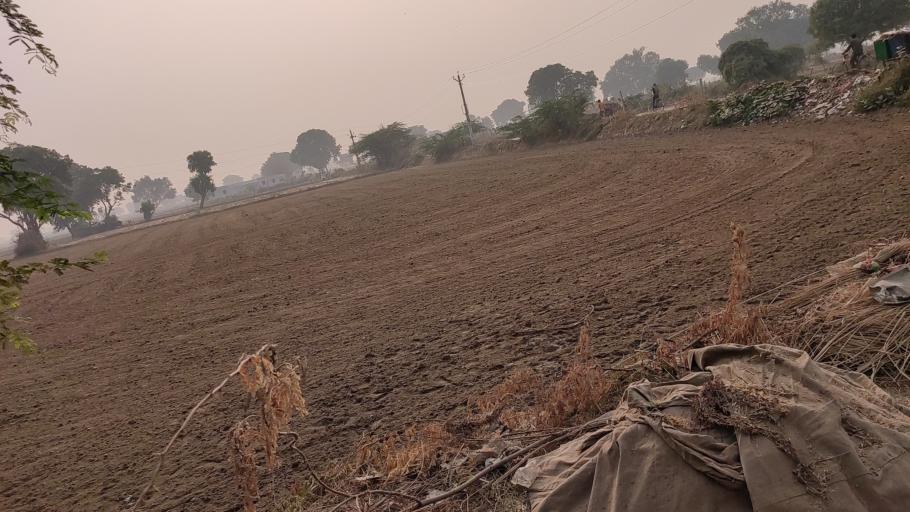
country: IN
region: Uttar Pradesh
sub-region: Mathura
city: Vrindavan
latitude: 27.5435
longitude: 77.7103
